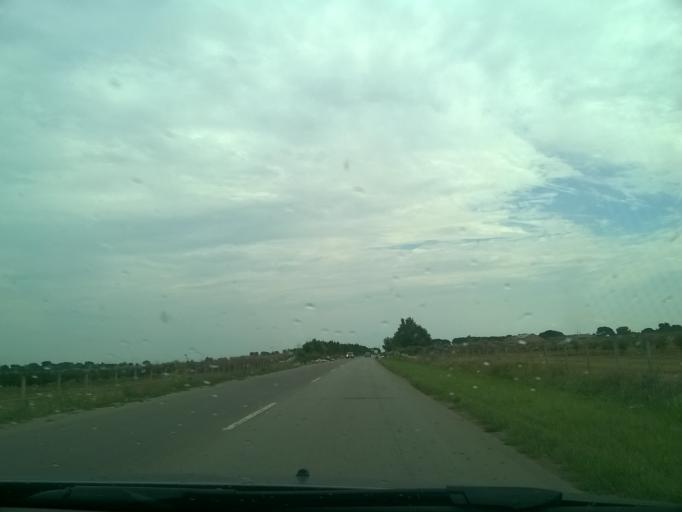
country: RS
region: Autonomna Pokrajina Vojvodina
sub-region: Srednjebanatski Okrug
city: Zrenjanin
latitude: 45.4019
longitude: 20.3838
